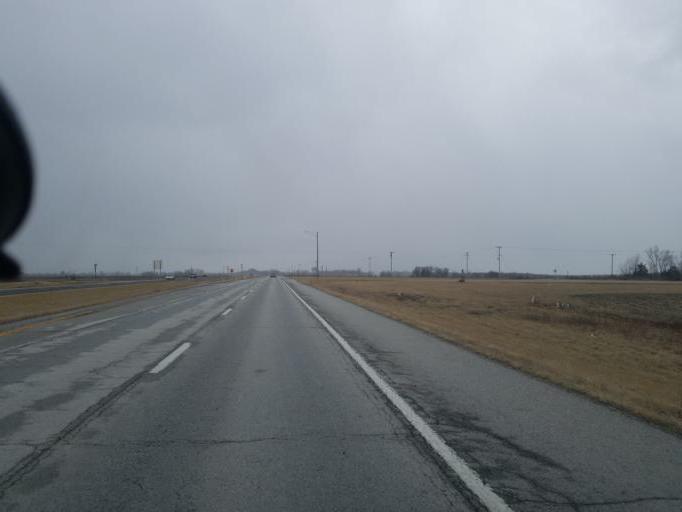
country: US
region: Missouri
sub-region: Macon County
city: La Plata
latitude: 39.8838
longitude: -92.4728
